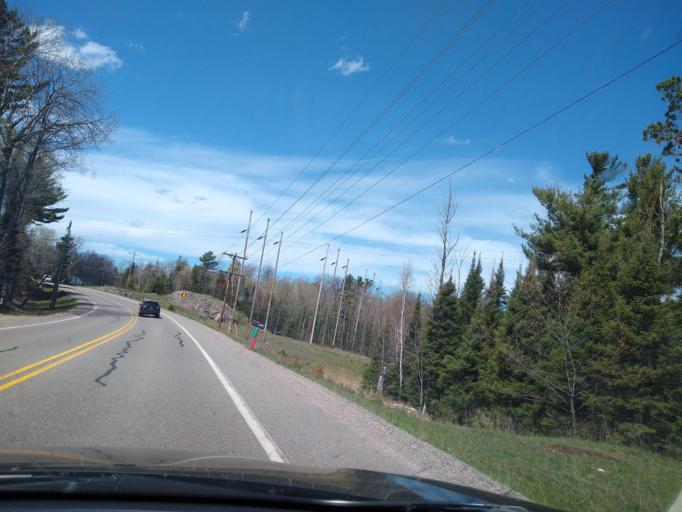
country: US
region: Michigan
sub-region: Marquette County
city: Trowbridge Park
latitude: 46.5776
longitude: -87.4237
